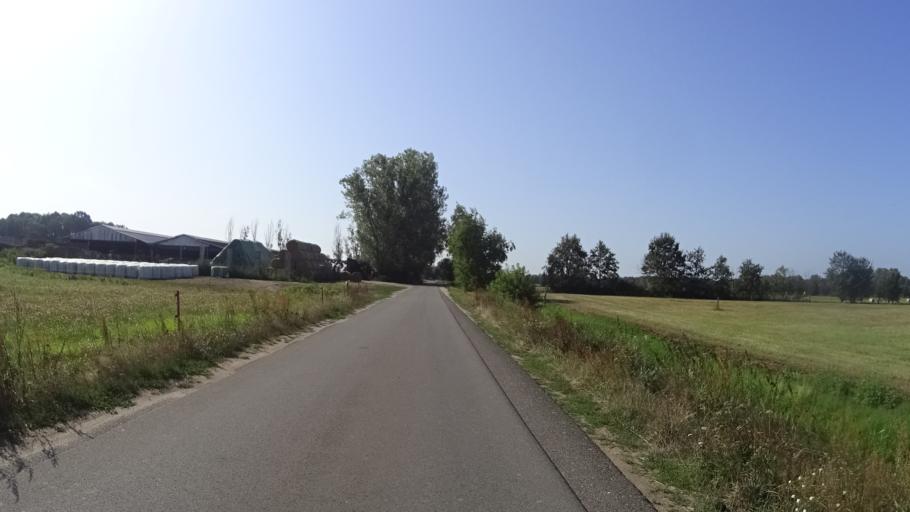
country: DE
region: Brandenburg
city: Straupitz
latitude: 51.8910
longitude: 14.1252
